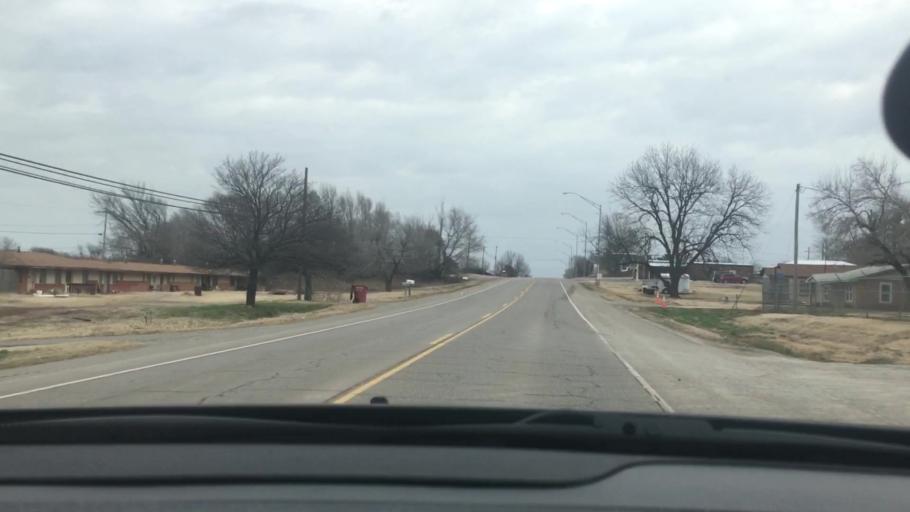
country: US
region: Oklahoma
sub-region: Garvin County
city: Maysville
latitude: 34.8190
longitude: -97.4242
